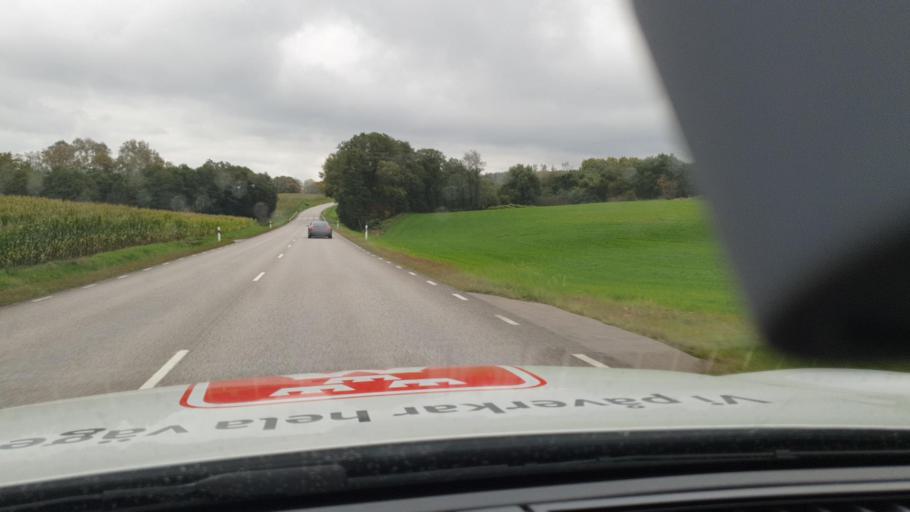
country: SE
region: Halland
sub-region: Falkenbergs Kommun
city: Falkenberg
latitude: 57.0245
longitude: 12.5977
